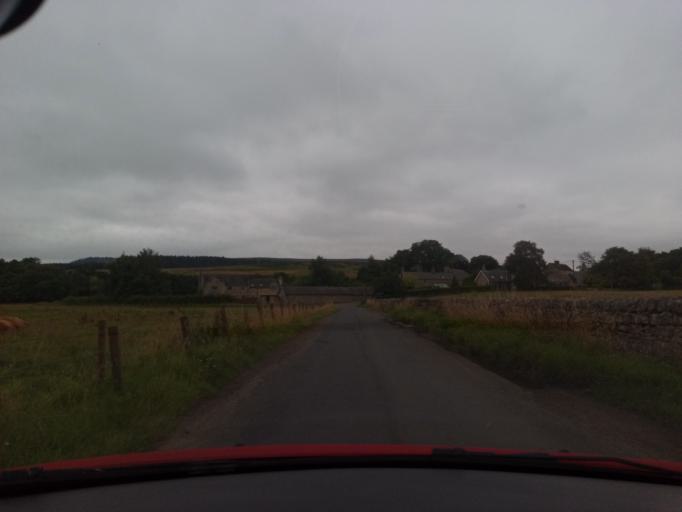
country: GB
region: England
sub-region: Northumberland
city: Otterburn
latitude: 55.3195
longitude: -2.0703
